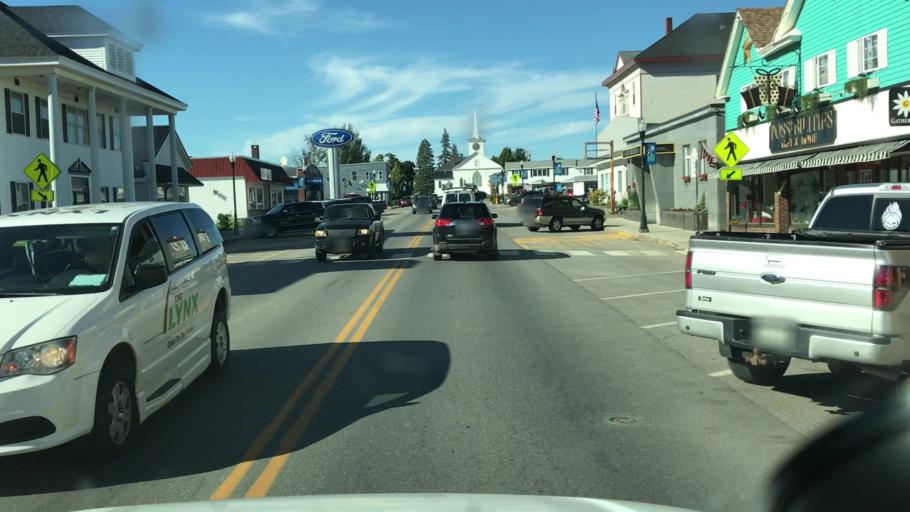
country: US
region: Maine
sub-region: Penobscot County
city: Lincoln
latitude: 45.3636
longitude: -68.5039
